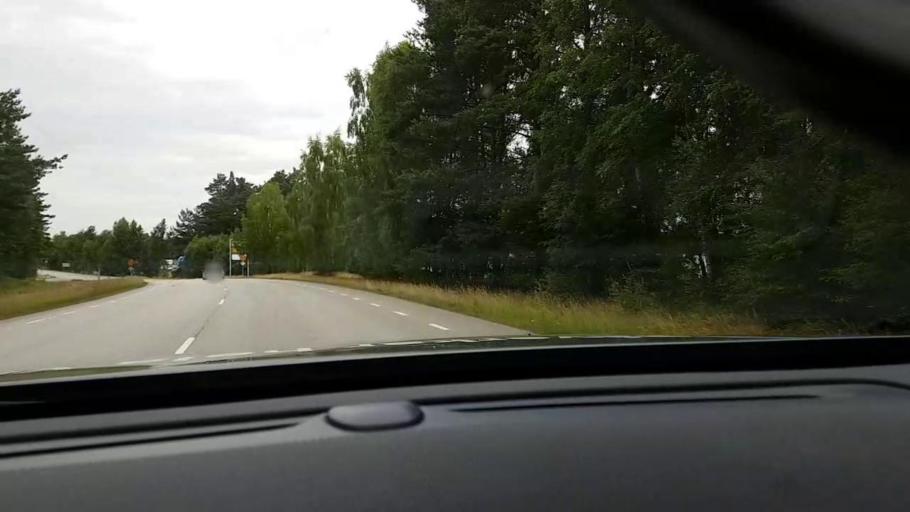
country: SE
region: Skane
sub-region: Hassleholms Kommun
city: Hassleholm
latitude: 56.1653
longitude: 13.8052
